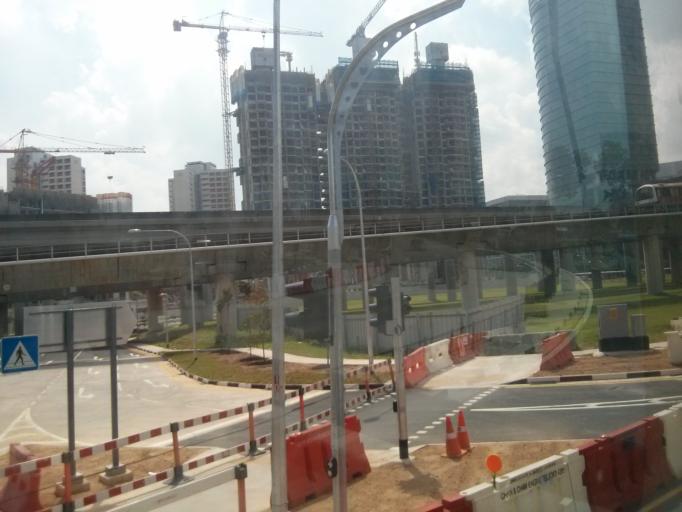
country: SG
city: Singapore
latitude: 1.3353
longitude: 103.7403
